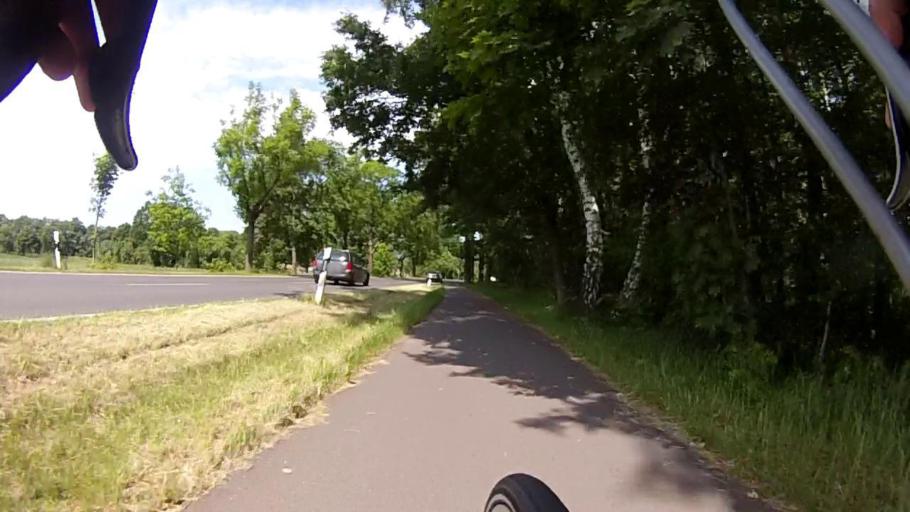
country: DE
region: Brandenburg
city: Liebenwalde
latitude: 52.8573
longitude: 13.3996
